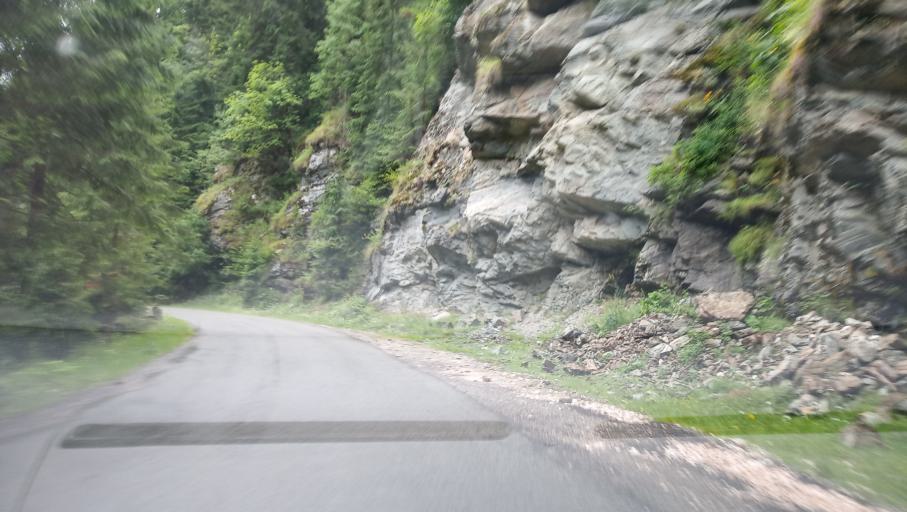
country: RO
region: Hunedoara
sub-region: Oras Petrila
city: Petrila
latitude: 45.4083
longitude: 23.5176
